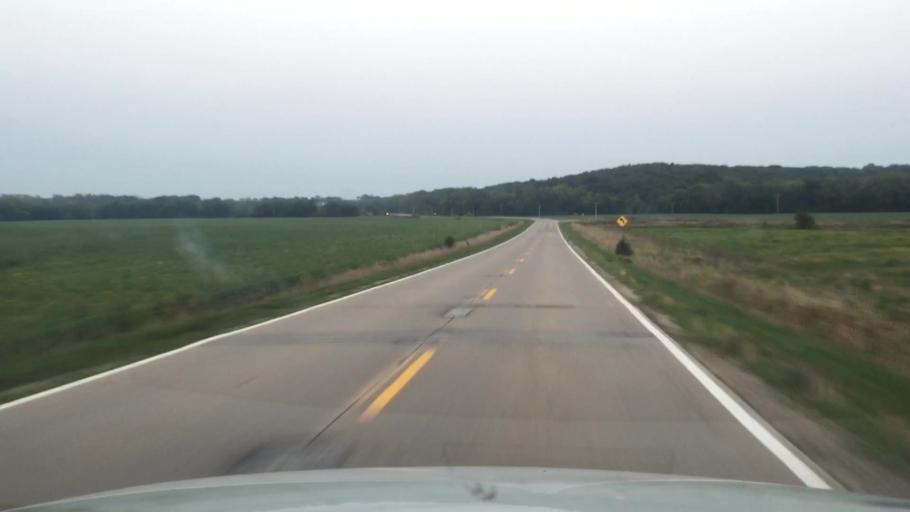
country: US
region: Iowa
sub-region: Warren County
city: Indianola
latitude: 41.1881
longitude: -93.6233
